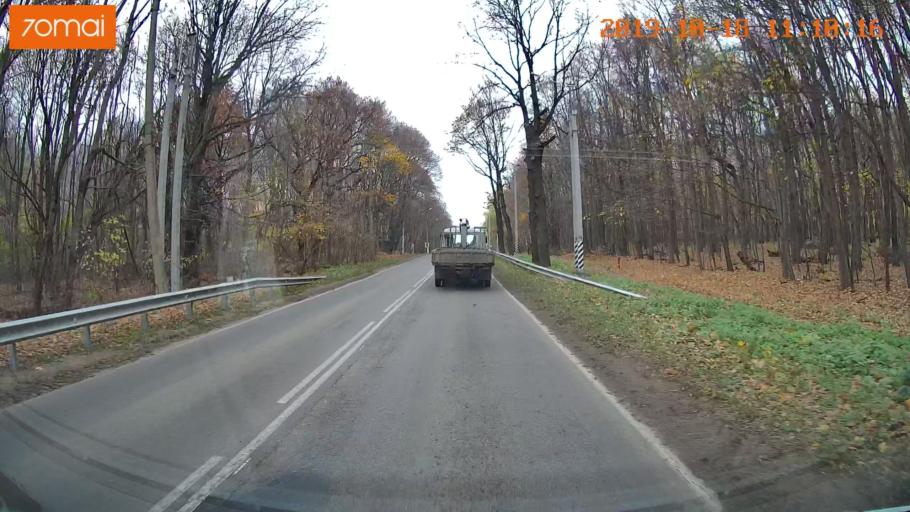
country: RU
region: Tula
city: Kimovsk
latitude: 53.9542
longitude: 38.5392
